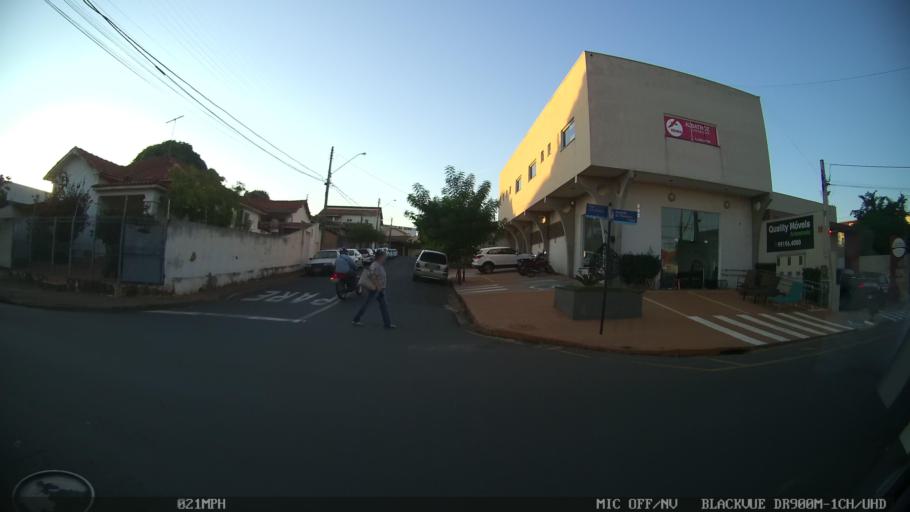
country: BR
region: Sao Paulo
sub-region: Sao Jose Do Rio Preto
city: Sao Jose do Rio Preto
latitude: -20.8043
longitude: -49.3653
